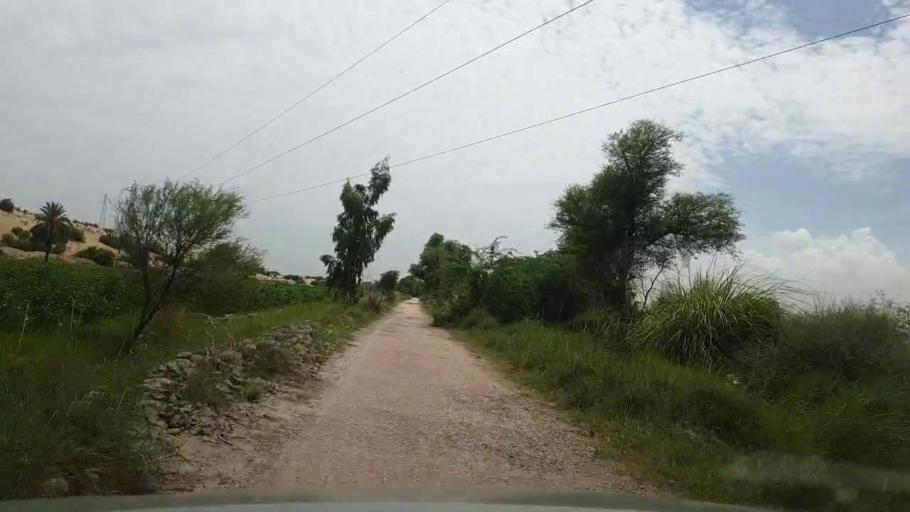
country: PK
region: Sindh
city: Bozdar
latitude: 27.0680
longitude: 68.9670
